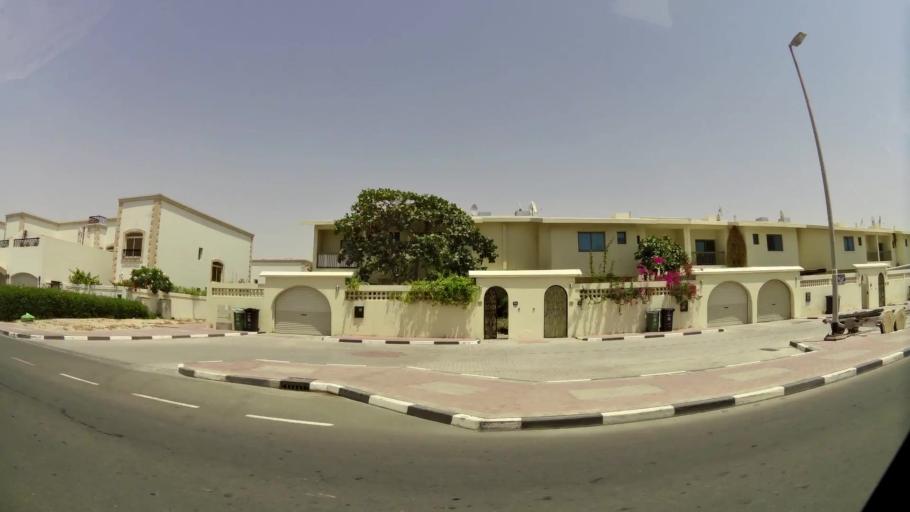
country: AE
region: Dubai
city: Dubai
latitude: 25.1377
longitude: 55.1984
